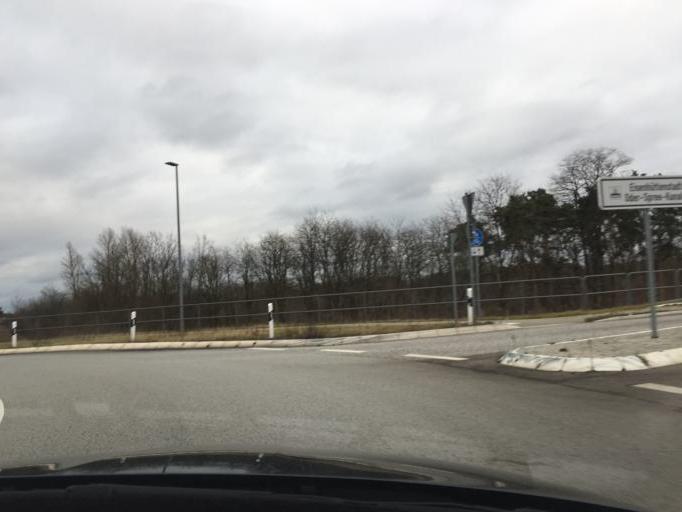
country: DE
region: Brandenburg
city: Ziltendorf
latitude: 52.1992
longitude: 14.6125
